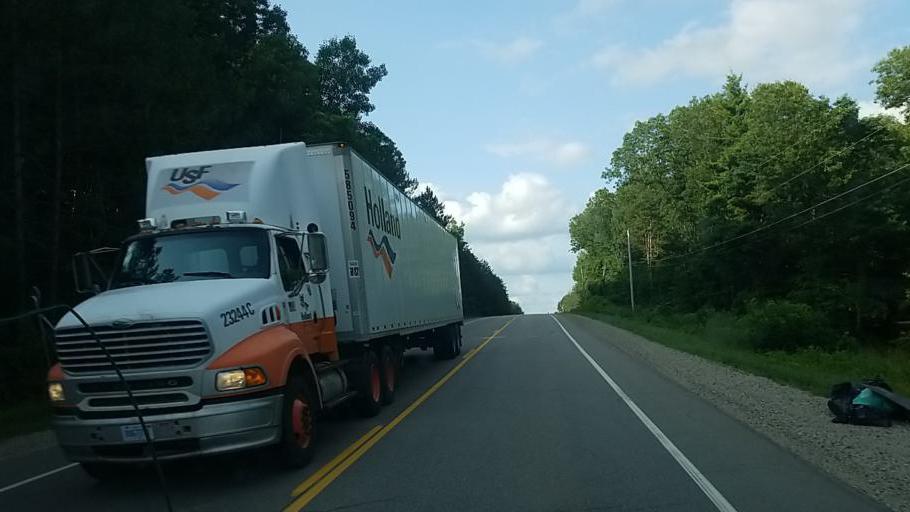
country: US
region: Michigan
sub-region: Kent County
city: Lowell
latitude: 42.9149
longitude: -85.3469
